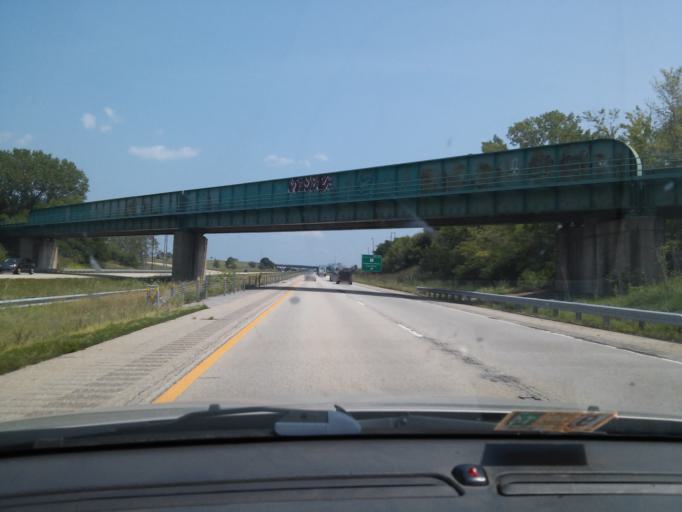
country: US
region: Illinois
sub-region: Sangamon County
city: Jerome
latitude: 39.7449
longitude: -89.7139
